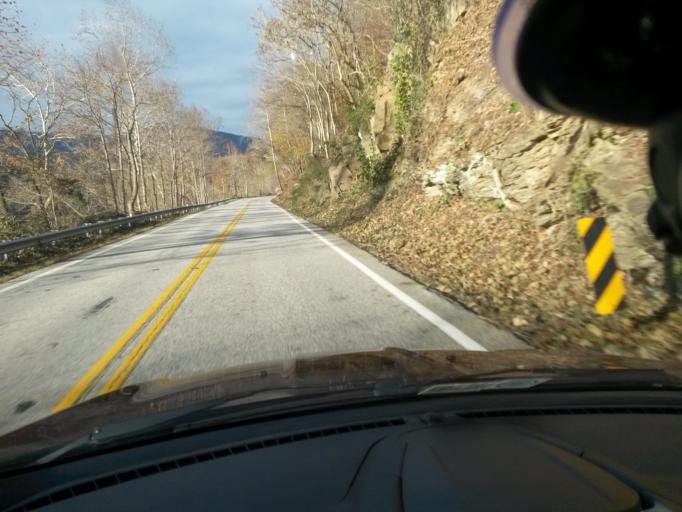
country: US
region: Virginia
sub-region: Rockbridge County
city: Glasgow
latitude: 37.5855
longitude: -79.3794
